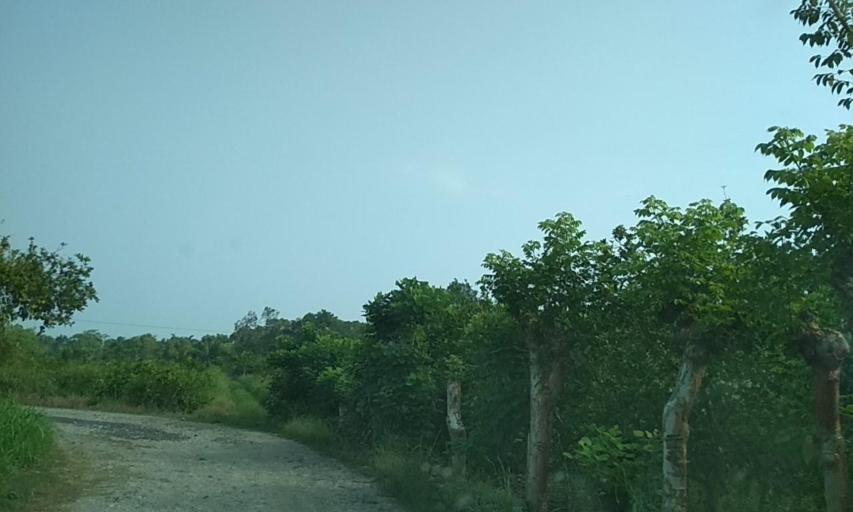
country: MX
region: Veracruz
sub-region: Misantla
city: La Defensa
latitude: 20.0497
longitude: -96.9806
